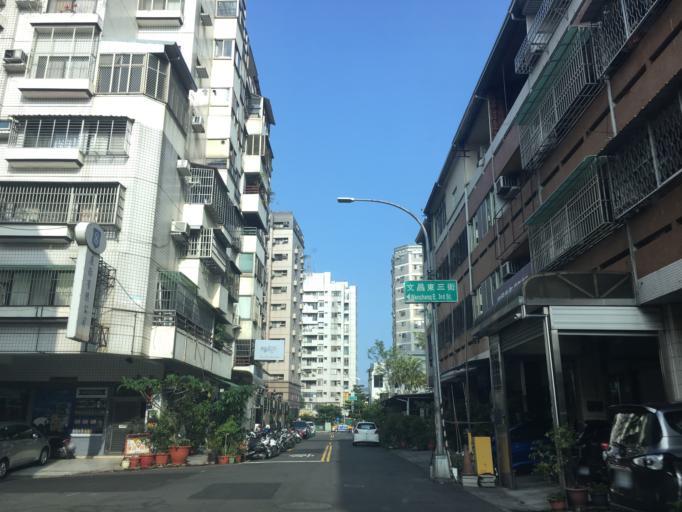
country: TW
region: Taiwan
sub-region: Taichung City
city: Taichung
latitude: 24.1719
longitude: 120.6808
